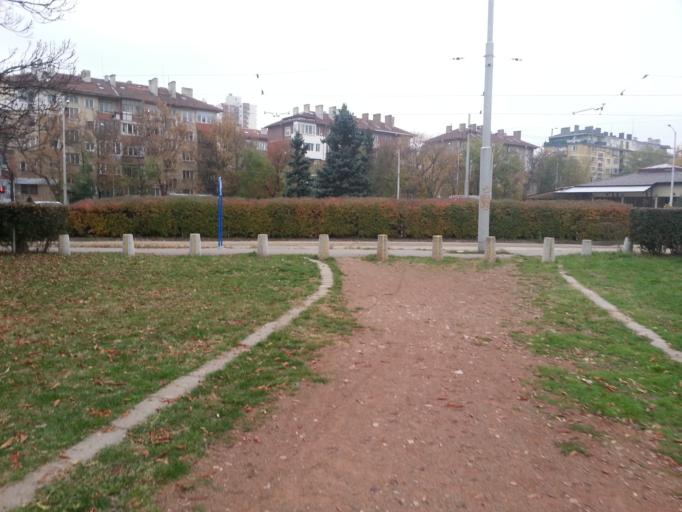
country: BG
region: Sofia-Capital
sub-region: Stolichna Obshtina
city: Sofia
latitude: 42.6760
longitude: 23.3146
